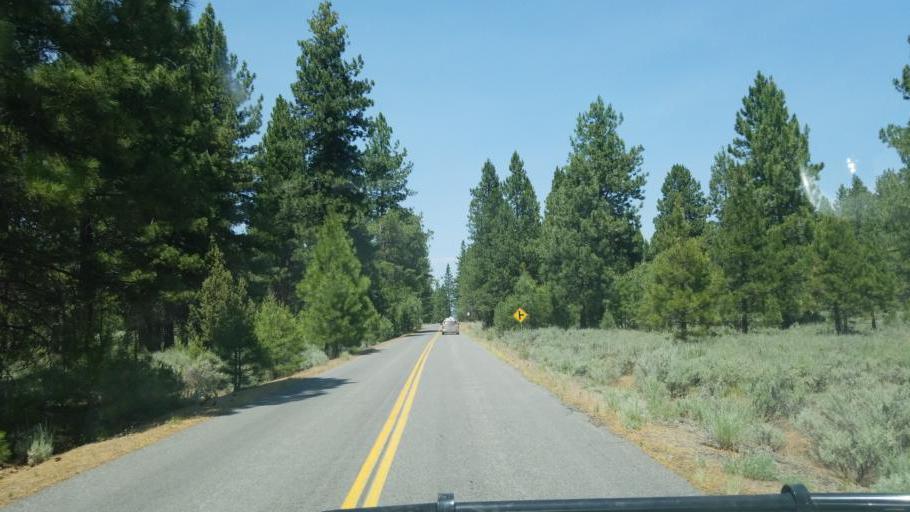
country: US
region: California
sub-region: Lassen County
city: Susanville
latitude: 40.5530
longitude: -120.7772
